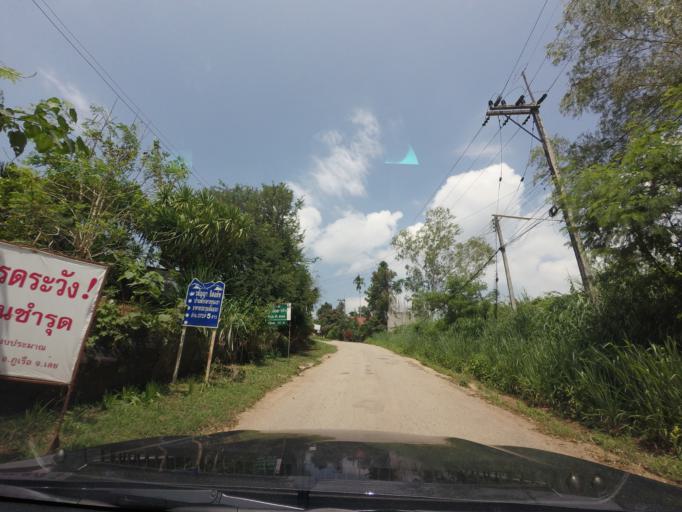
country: TH
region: Loei
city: Phu Ruea
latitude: 17.4575
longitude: 101.3589
